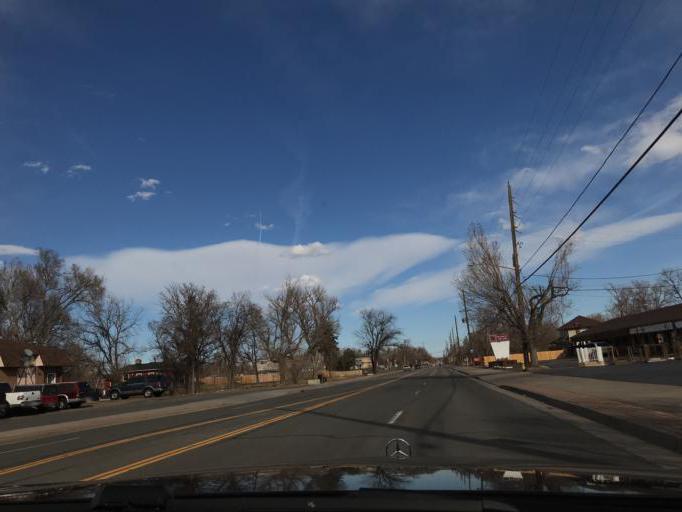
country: US
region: Colorado
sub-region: Jefferson County
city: Applewood
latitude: 39.7782
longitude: -105.1306
